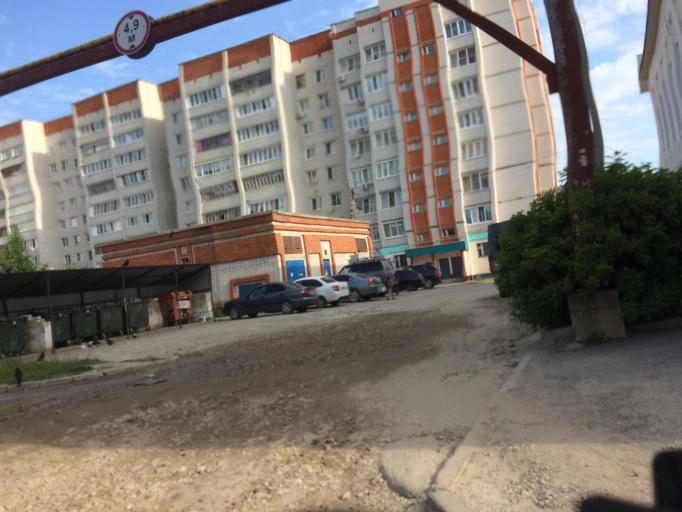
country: RU
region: Mariy-El
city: Medvedevo
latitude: 56.6388
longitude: 47.8282
